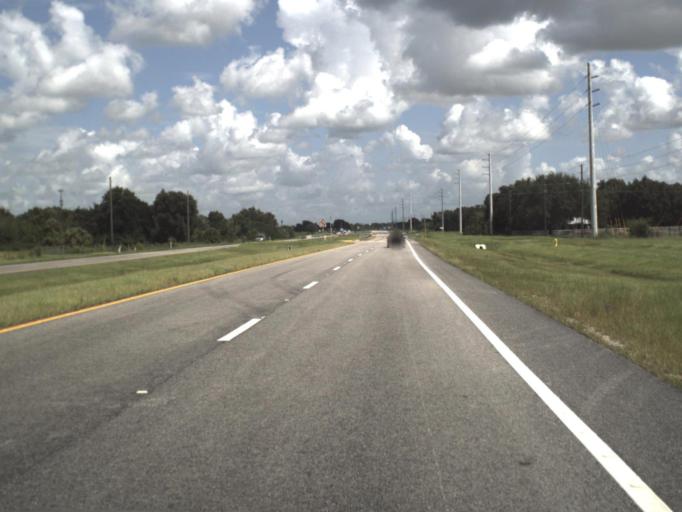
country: US
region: Florida
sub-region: Charlotte County
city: Harbour Heights
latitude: 27.0611
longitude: -81.9581
